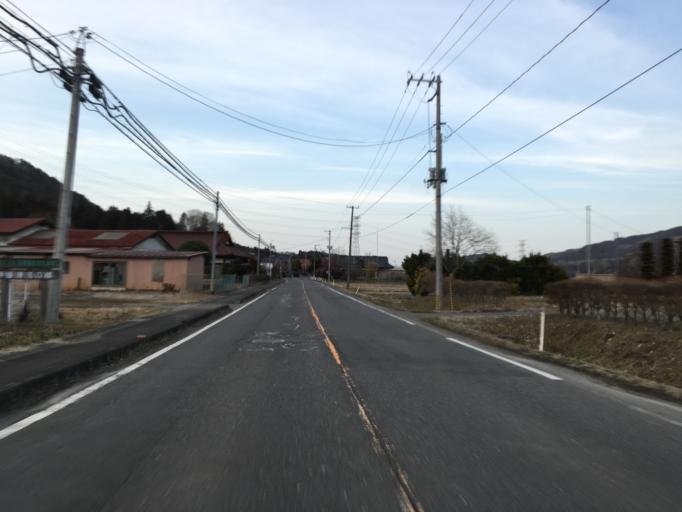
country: JP
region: Ibaraki
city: Daigo
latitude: 36.9193
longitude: 140.4080
